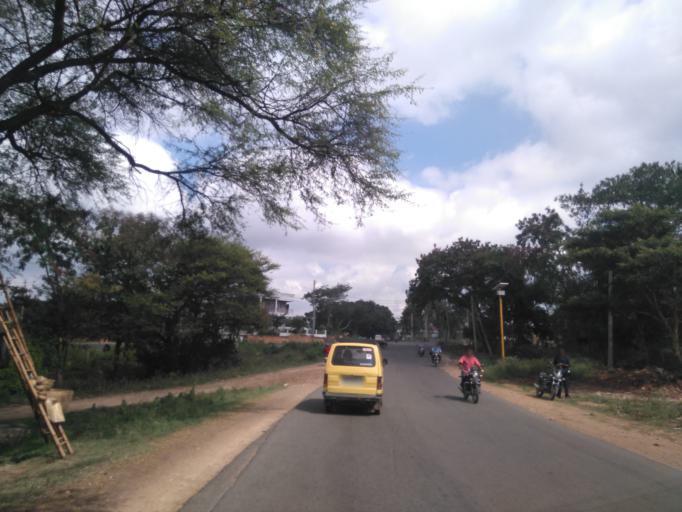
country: IN
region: Karnataka
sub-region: Mysore
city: Mysore
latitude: 12.2926
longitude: 76.7063
